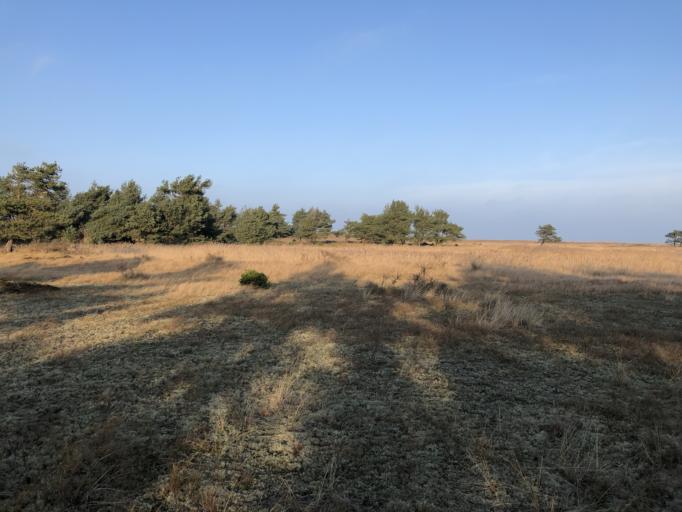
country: DE
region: Mecklenburg-Vorpommern
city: Ostseebad Prerow
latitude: 54.4798
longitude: 12.5141
